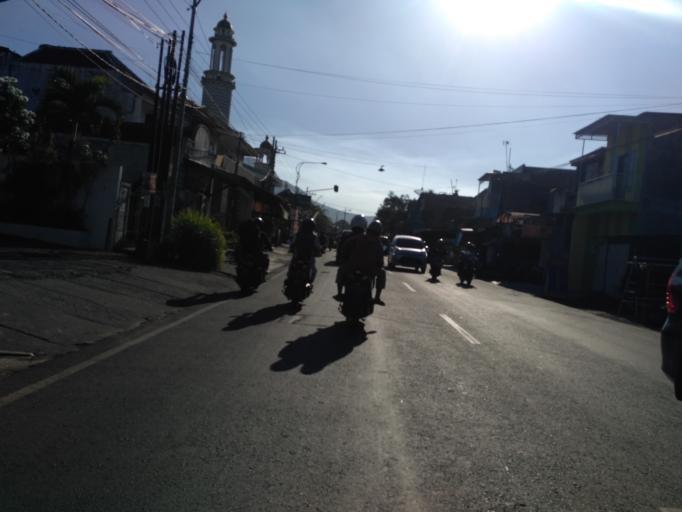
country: ID
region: East Java
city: Malang
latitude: -7.9193
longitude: 112.5920
